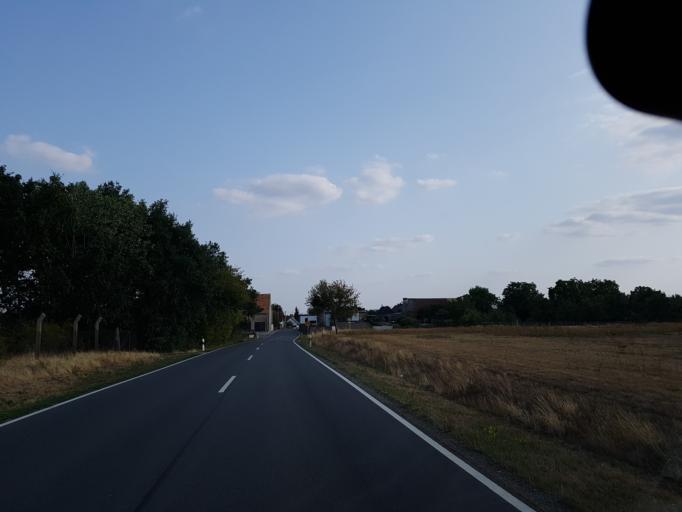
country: DE
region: Saxony
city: Dommitzsch
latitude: 51.6583
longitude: 12.8580
